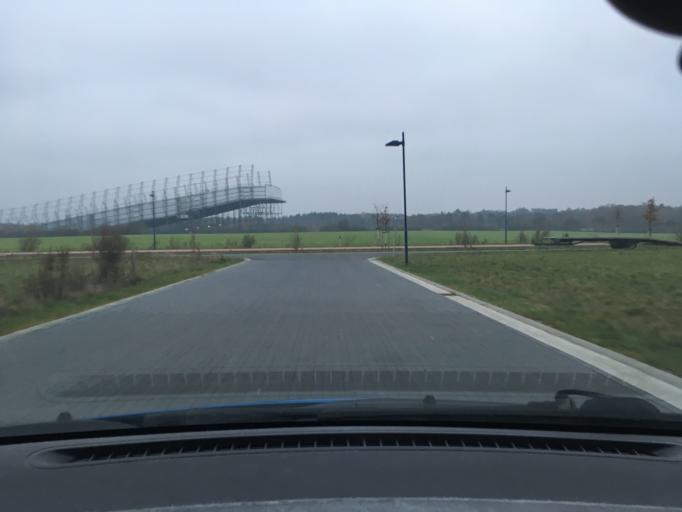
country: DE
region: Lower Saxony
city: Bispingen
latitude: 53.0989
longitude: 9.9867
